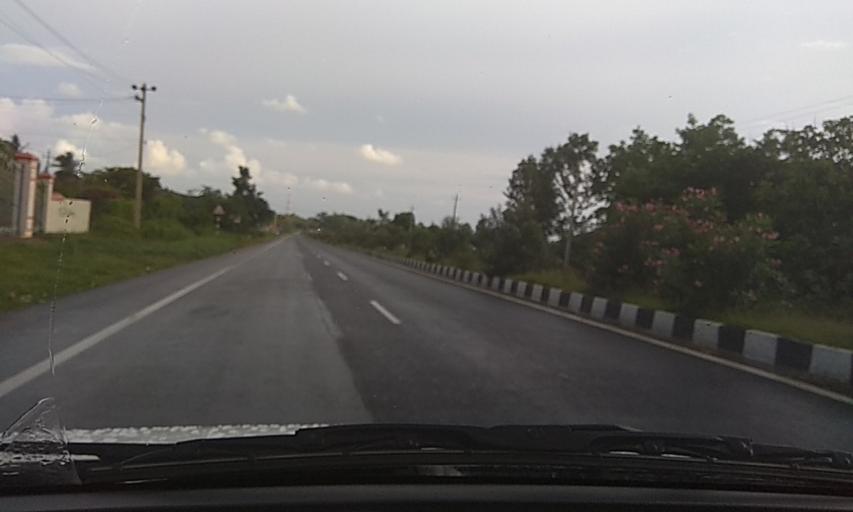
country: IN
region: Karnataka
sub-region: Mysore
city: Nanjangud
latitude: 12.1759
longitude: 76.6714
